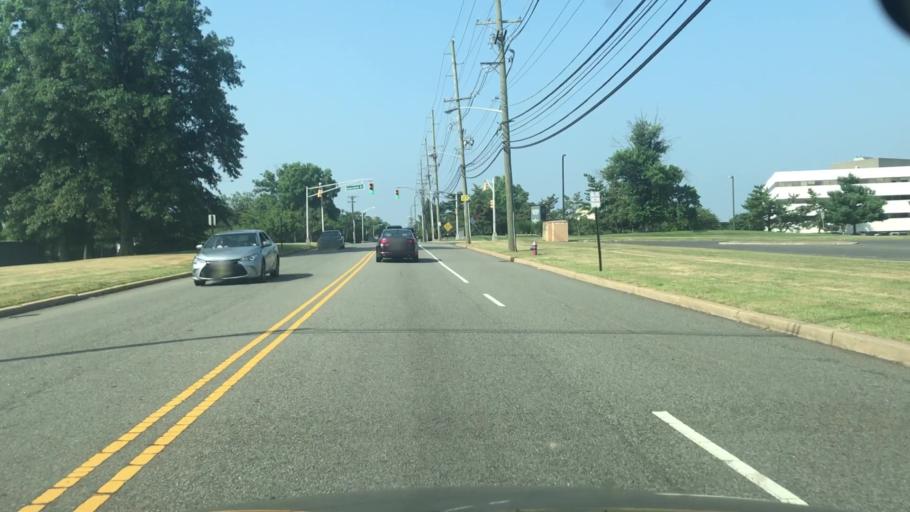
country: US
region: New Jersey
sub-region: Somerset County
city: South Bound Brook
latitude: 40.5414
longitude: -74.5195
